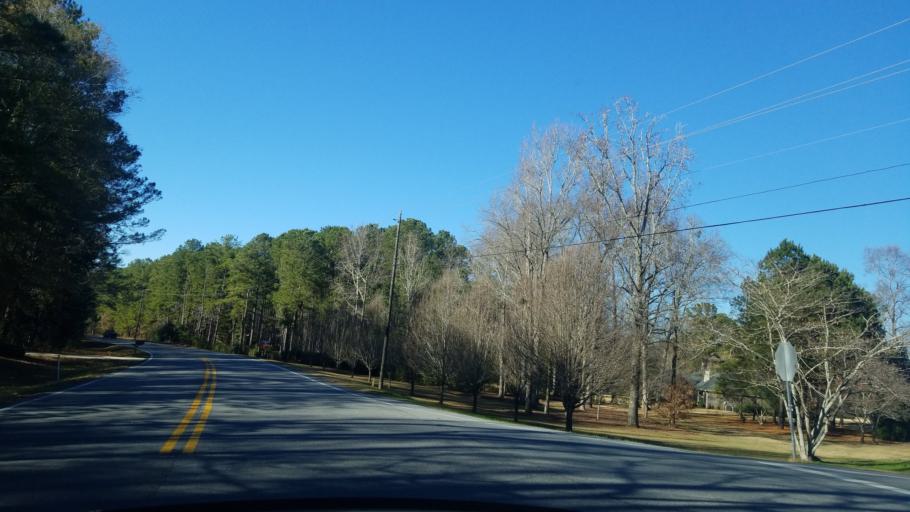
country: US
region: Georgia
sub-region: Harris County
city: Hamilton
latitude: 32.6736
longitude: -84.9073
